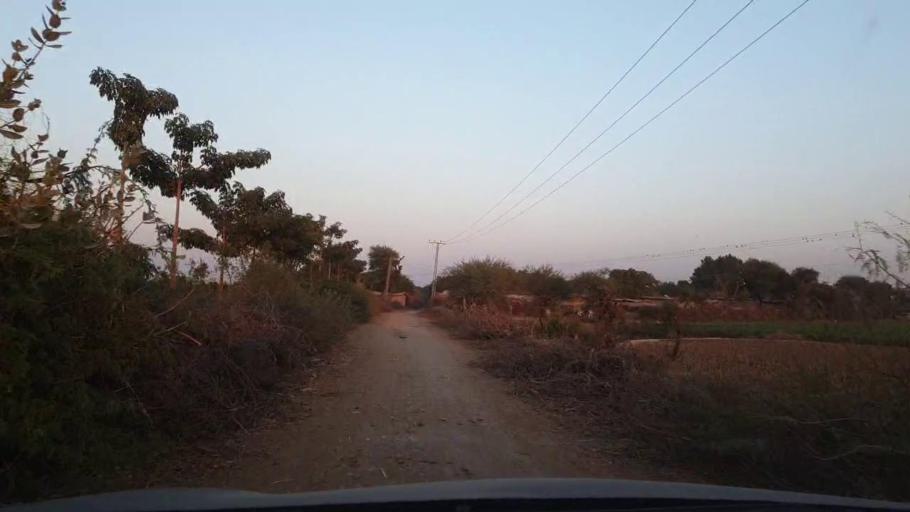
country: PK
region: Sindh
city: Tando Allahyar
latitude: 25.5055
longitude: 68.7471
